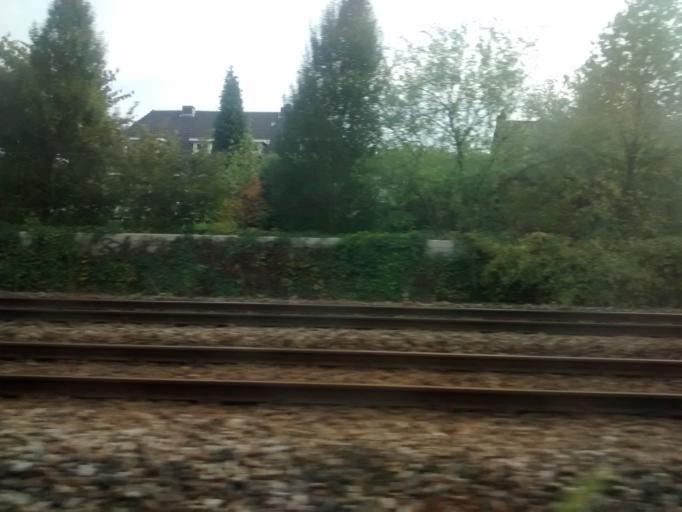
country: NL
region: North Brabant
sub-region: Gemeente 's-Hertogenbosch
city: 's-Hertogenbosch
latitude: 51.6799
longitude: 5.2908
